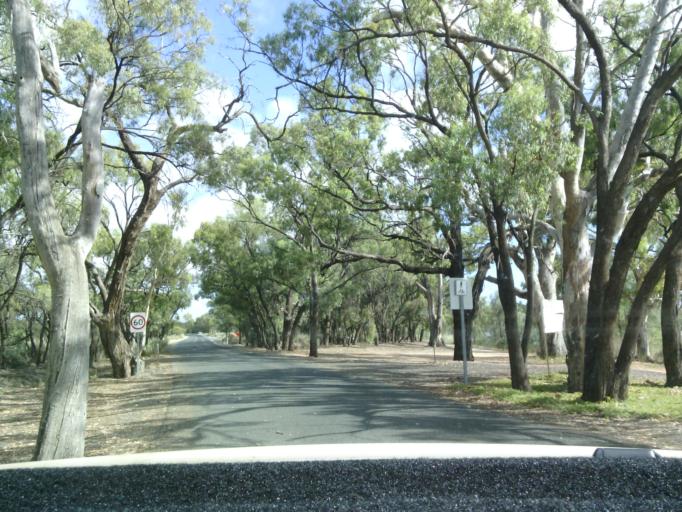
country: AU
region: South Australia
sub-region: Berri and Barmera
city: Berri
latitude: -34.2859
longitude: 140.6314
